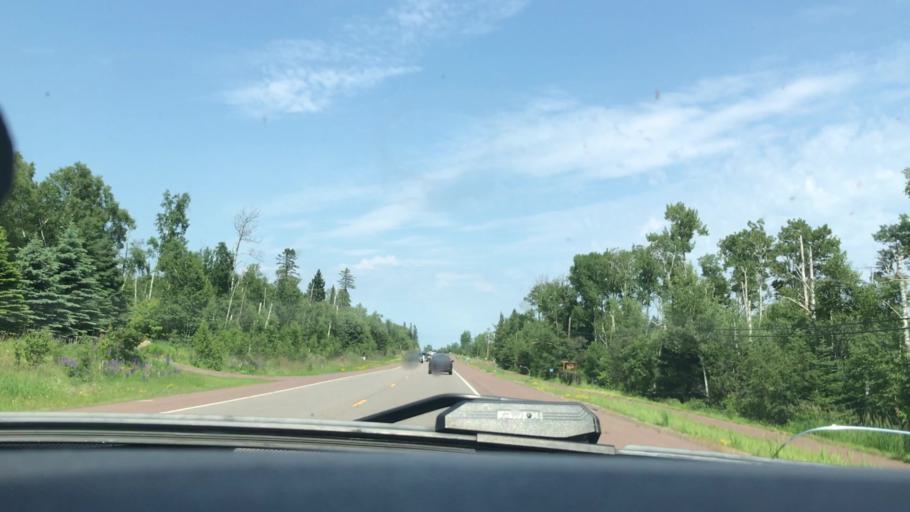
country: US
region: Minnesota
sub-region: Cook County
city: Grand Marais
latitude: 47.5899
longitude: -90.8057
